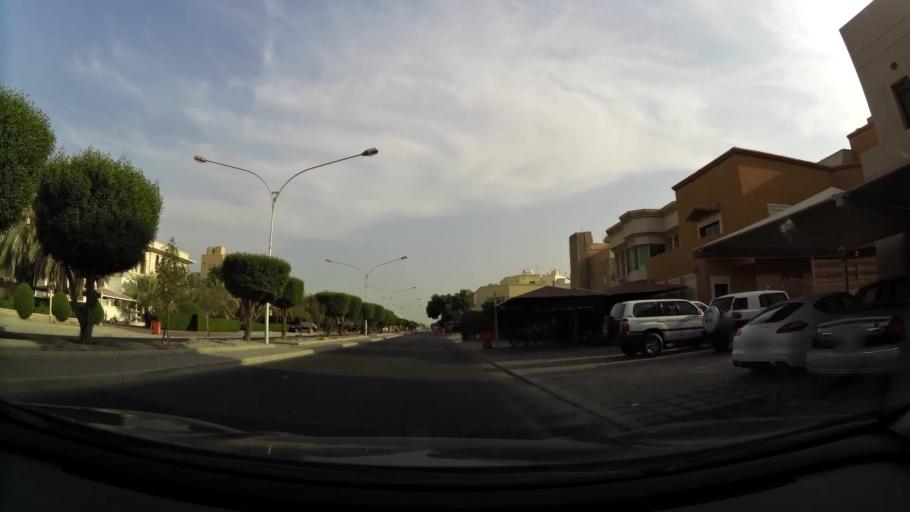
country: KW
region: Muhafazat Hawalli
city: Hawalli
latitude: 29.3172
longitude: 48.0082
